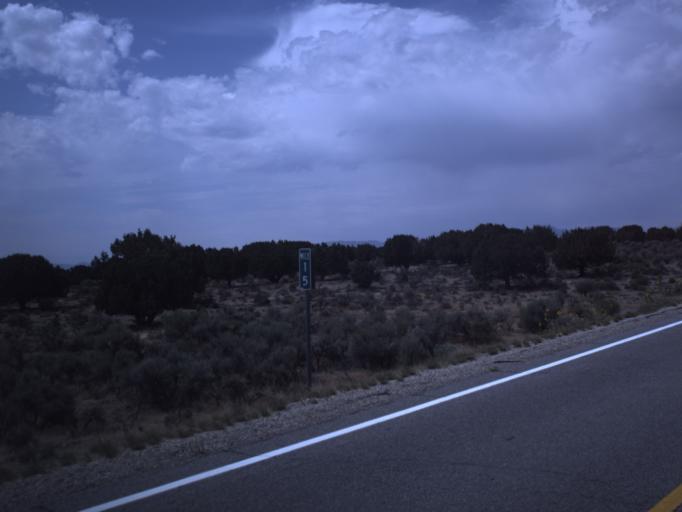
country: US
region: Utah
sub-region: Utah County
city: Eagle Mountain
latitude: 40.2327
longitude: -112.1932
